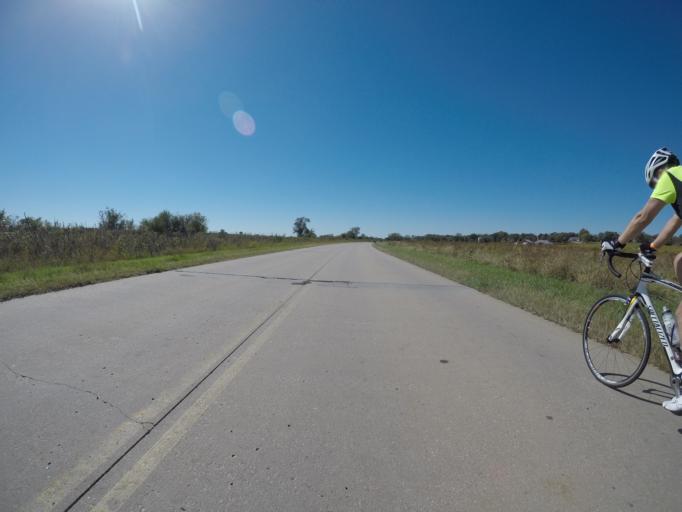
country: US
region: Kansas
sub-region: Wyandotte County
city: Bonner Springs
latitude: 39.0195
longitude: -94.9024
